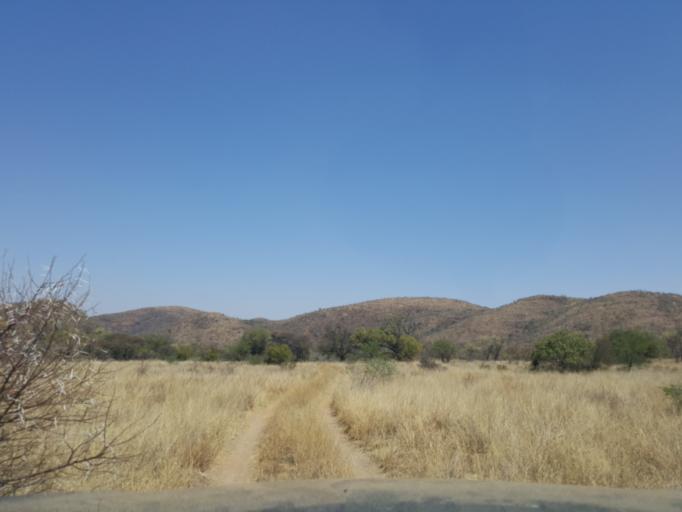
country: BW
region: South East
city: Lobatse
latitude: -25.1386
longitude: 25.6716
